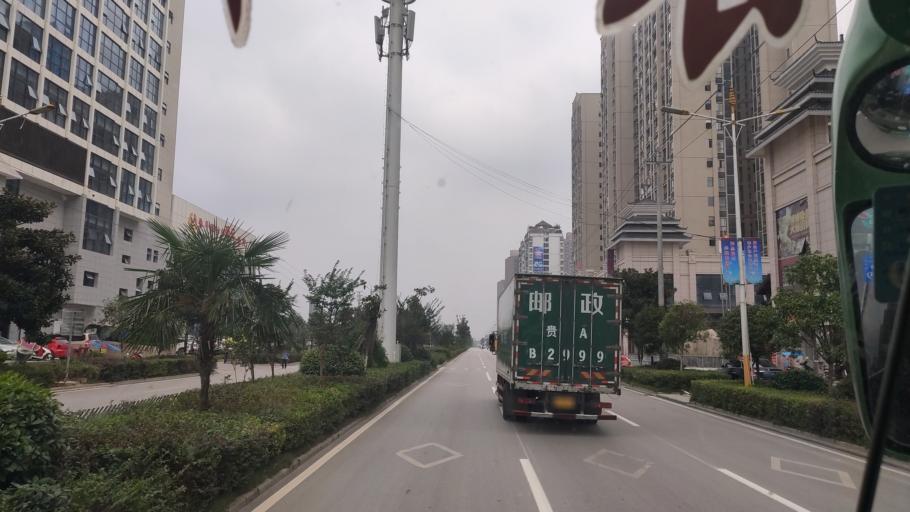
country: CN
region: Guizhou Sheng
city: Zhongchao
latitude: 26.2141
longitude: 109.1163
